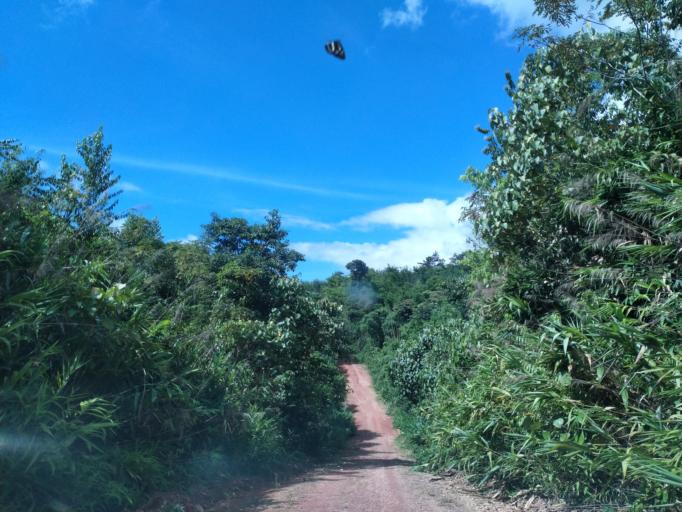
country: LA
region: Vientiane
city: Muang Phon-Hong
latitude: 18.6447
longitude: 102.8990
